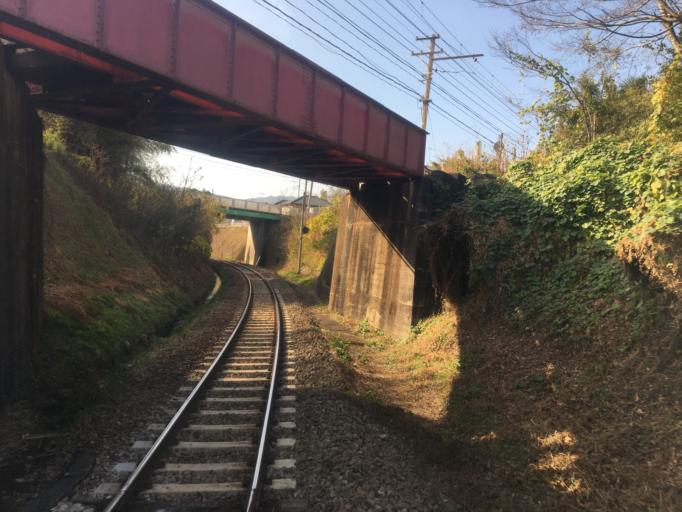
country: JP
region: Saitama
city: Yorii
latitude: 36.1171
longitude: 139.1874
